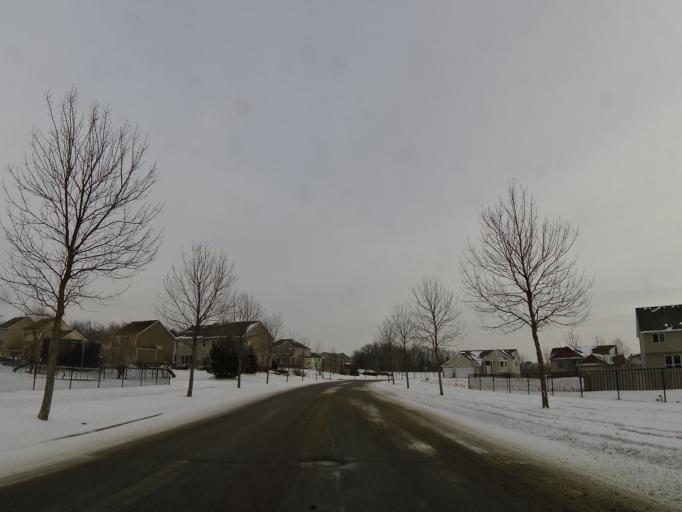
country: US
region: Minnesota
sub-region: Hennepin County
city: Saint Bonifacius
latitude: 44.8975
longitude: -93.7615
